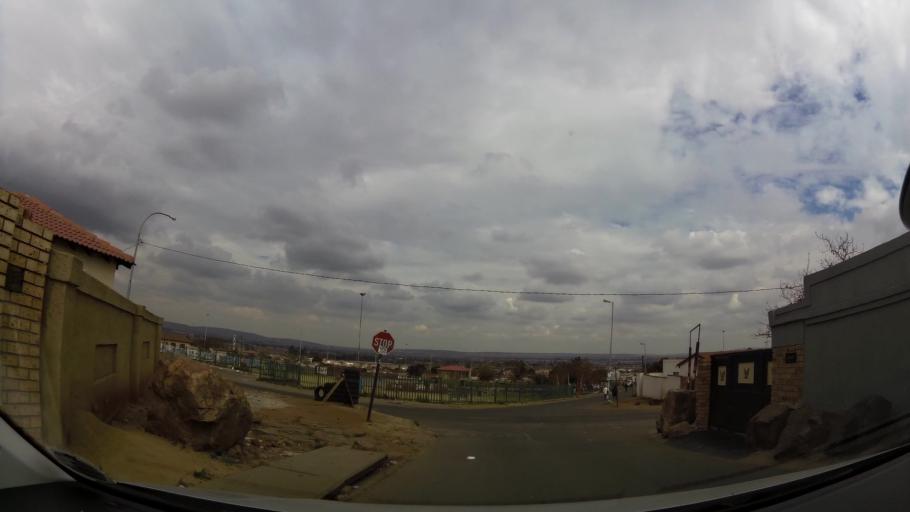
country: ZA
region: Gauteng
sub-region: City of Johannesburg Metropolitan Municipality
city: Soweto
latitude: -26.2803
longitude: 27.8585
